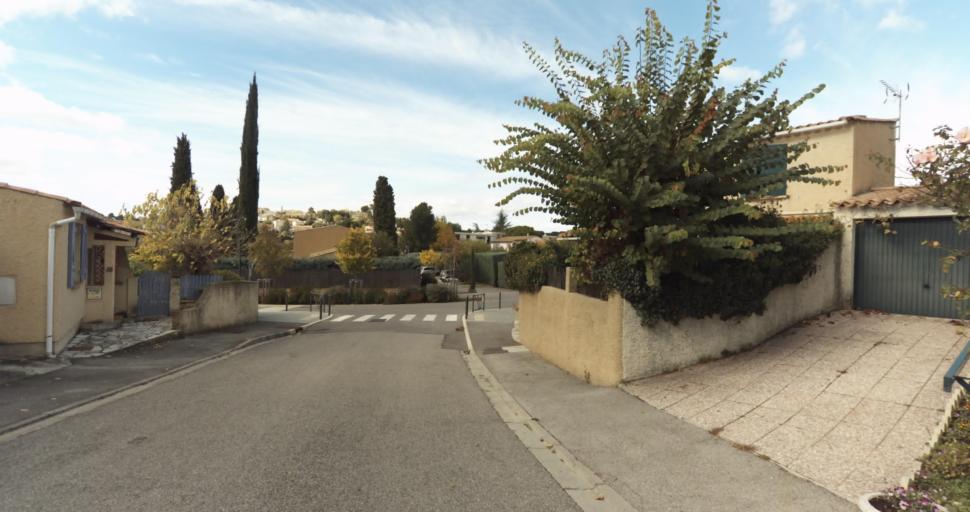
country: FR
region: Provence-Alpes-Cote d'Azur
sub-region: Departement des Bouches-du-Rhone
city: Venelles
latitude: 43.5986
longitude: 5.4884
